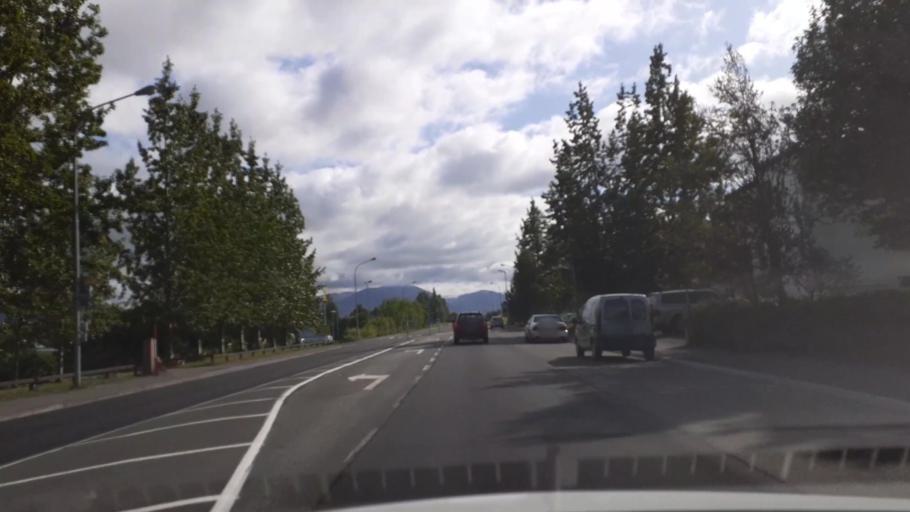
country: IS
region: Northeast
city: Akureyri
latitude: 65.6764
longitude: -18.0983
